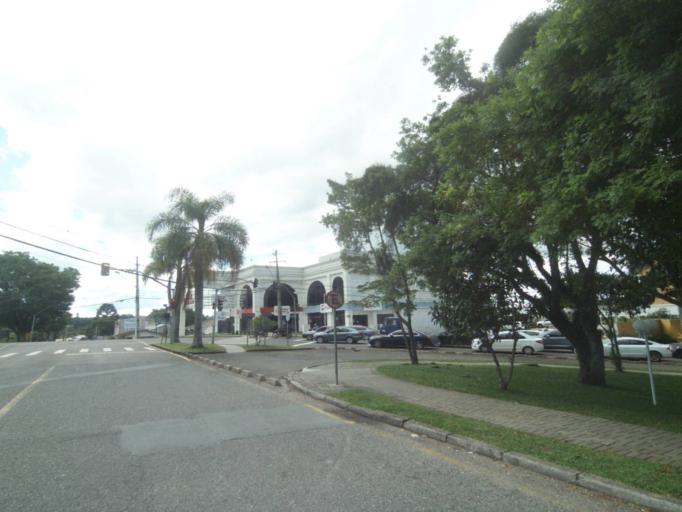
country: BR
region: Parana
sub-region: Curitiba
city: Curitiba
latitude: -25.4377
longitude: -49.3353
